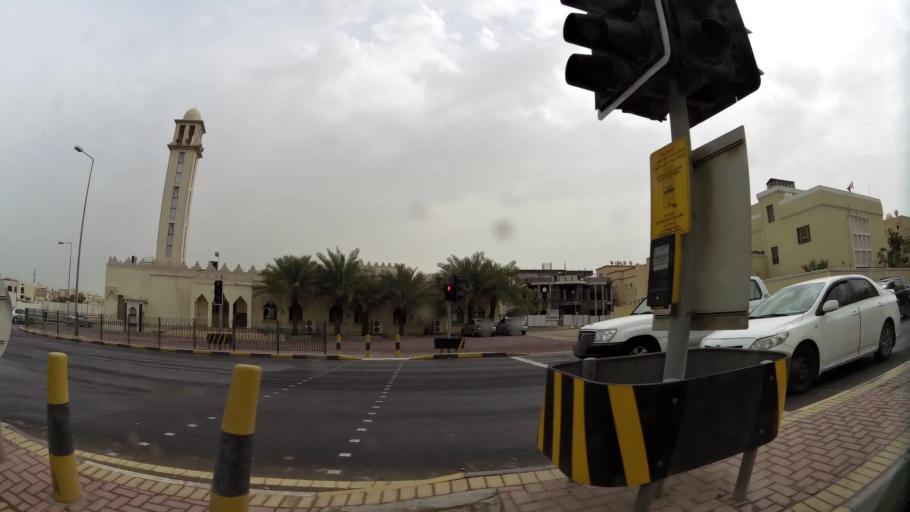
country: BH
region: Northern
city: Ar Rifa'
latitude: 26.1347
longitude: 50.5472
